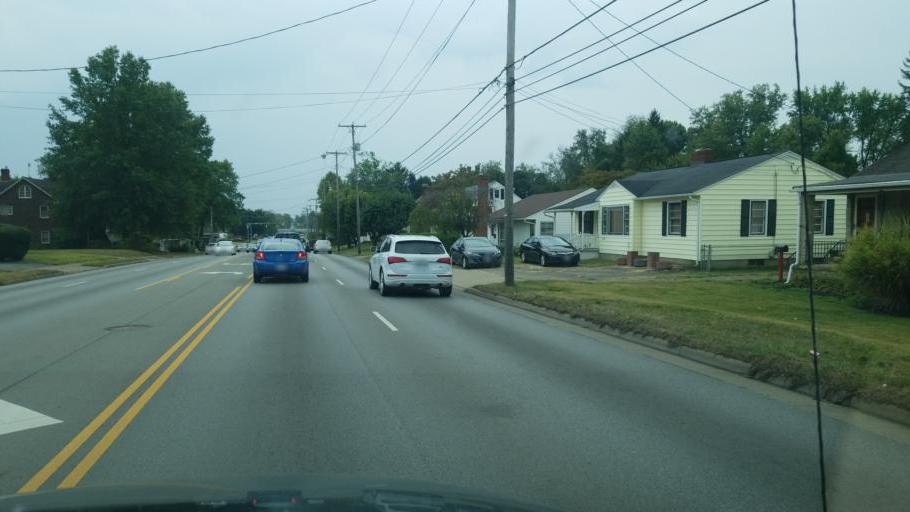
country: US
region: Ohio
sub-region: Licking County
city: Newark
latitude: 40.0682
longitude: -82.4292
